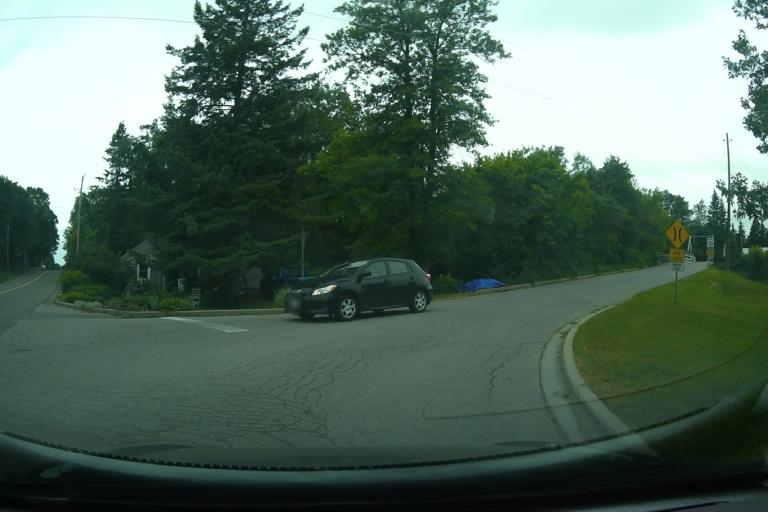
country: CA
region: Ontario
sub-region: Lanark County
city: Smiths Falls
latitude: 44.9800
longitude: -75.7959
